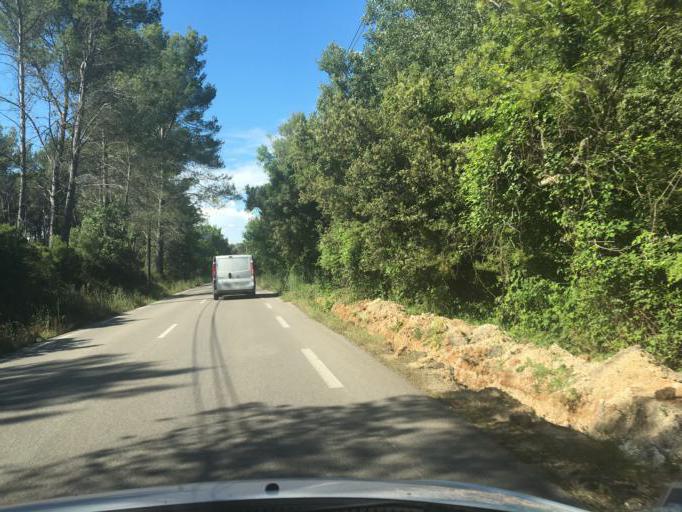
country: FR
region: Provence-Alpes-Cote d'Azur
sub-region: Departement des Bouches-du-Rhone
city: Eguilles
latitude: 43.5254
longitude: 5.3517
